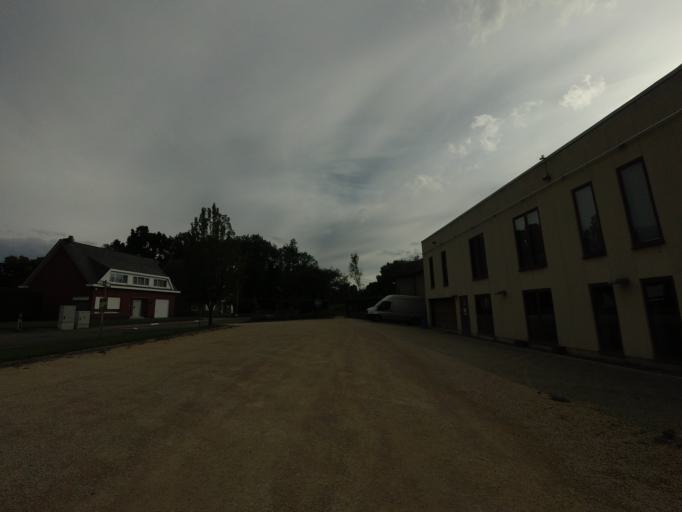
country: BE
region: Flanders
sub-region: Provincie Vlaams-Brabant
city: Boortmeerbeek
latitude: 50.9814
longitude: 4.5435
